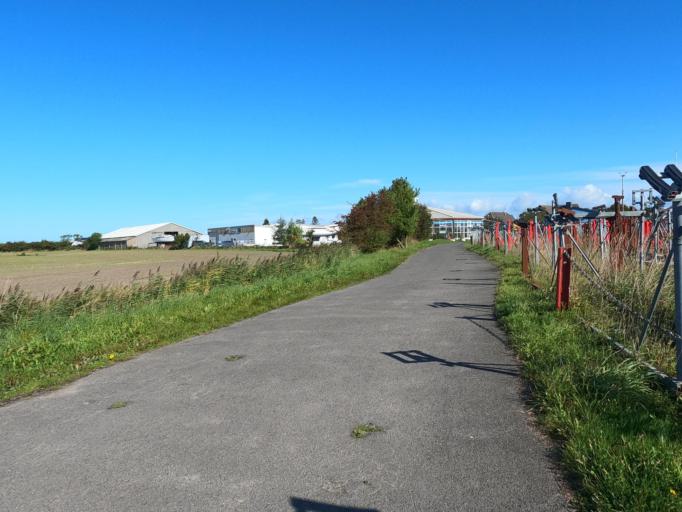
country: DE
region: Schleswig-Holstein
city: Grossenbrode
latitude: 54.3574
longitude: 11.0600
